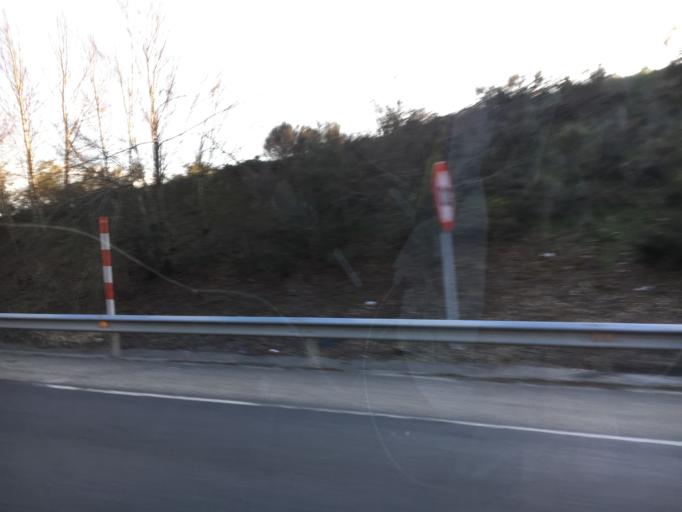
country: ES
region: Galicia
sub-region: Provincia de Lugo
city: San Roman
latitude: 42.7401
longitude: -7.0482
